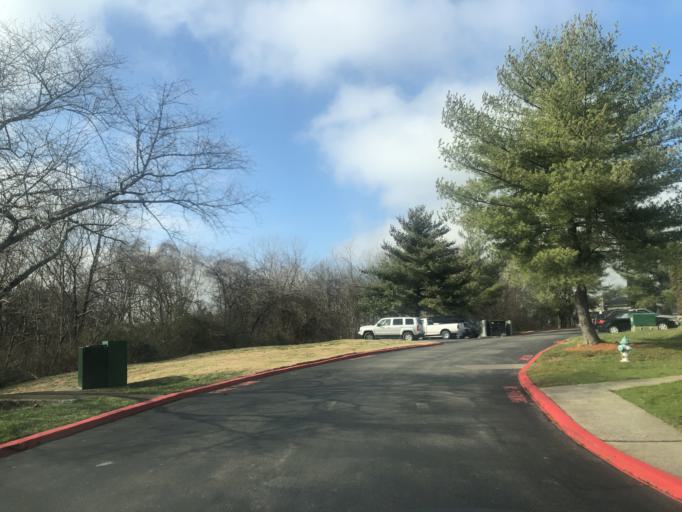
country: US
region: Tennessee
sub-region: Rutherford County
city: La Vergne
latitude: 36.0792
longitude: -86.6609
